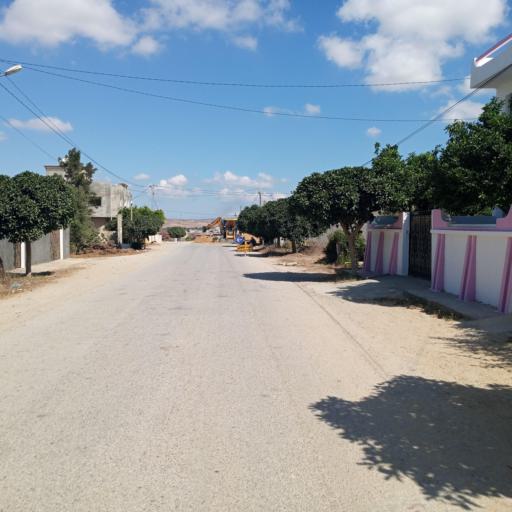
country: TN
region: Nabul
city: Qulaybiyah
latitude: 36.8558
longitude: 11.0359
